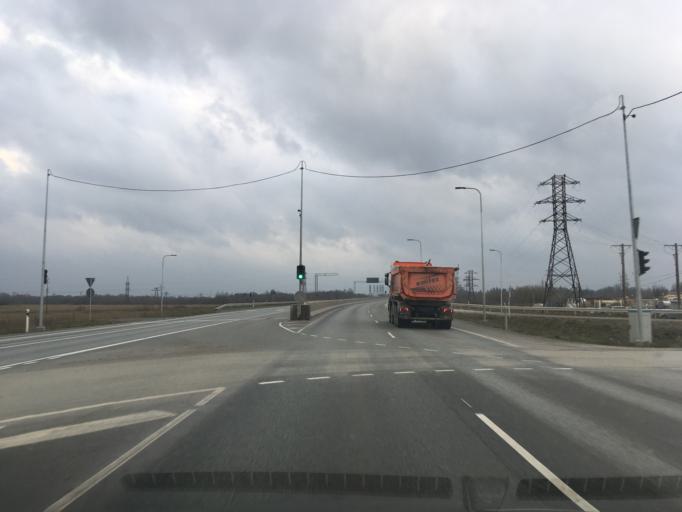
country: EE
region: Harju
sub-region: Joelaehtme vald
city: Loo
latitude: 59.4315
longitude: 24.9189
